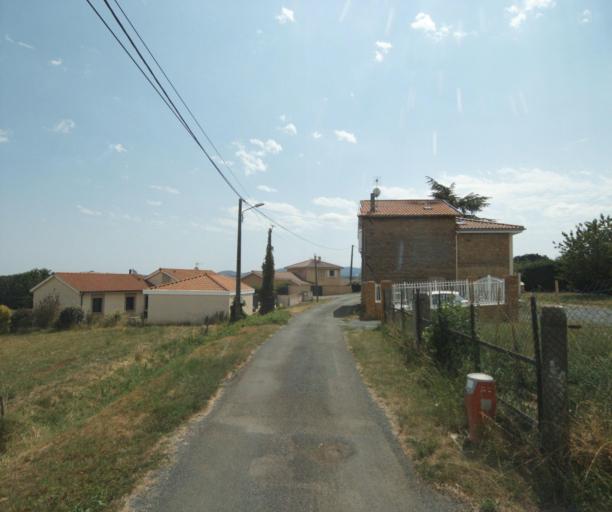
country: FR
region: Rhone-Alpes
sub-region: Departement du Rhone
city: Saint-Germain-Nuelles
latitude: 45.8619
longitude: 4.6093
